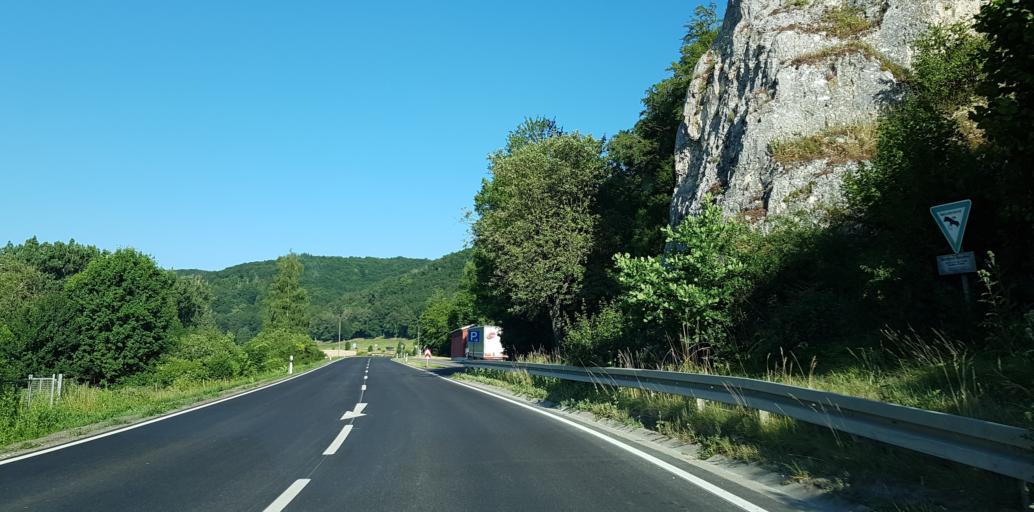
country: DE
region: Baden-Wuerttemberg
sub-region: Tuebingen Region
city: Blaubeuren
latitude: 48.4106
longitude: 9.8486
